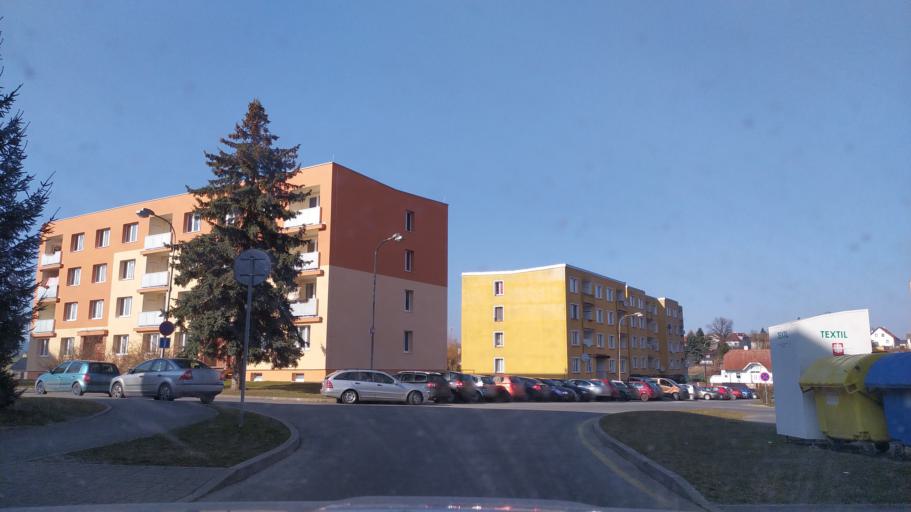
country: CZ
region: Karlovarsky
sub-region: Okres Cheb
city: Frantiskovy Lazne
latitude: 50.1269
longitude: 12.3403
